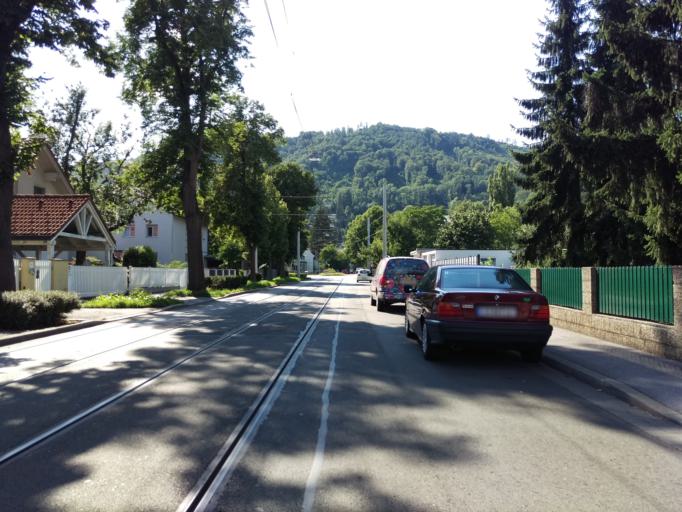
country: AT
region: Styria
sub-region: Graz Stadt
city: Wetzelsdorf
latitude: 47.0693
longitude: 15.3955
